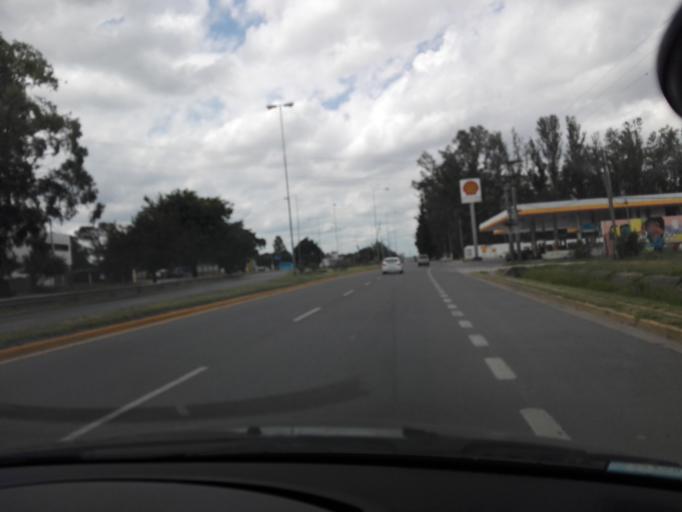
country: AR
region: Cordoba
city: Alta Gracia
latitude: -31.6520
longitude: -64.4085
